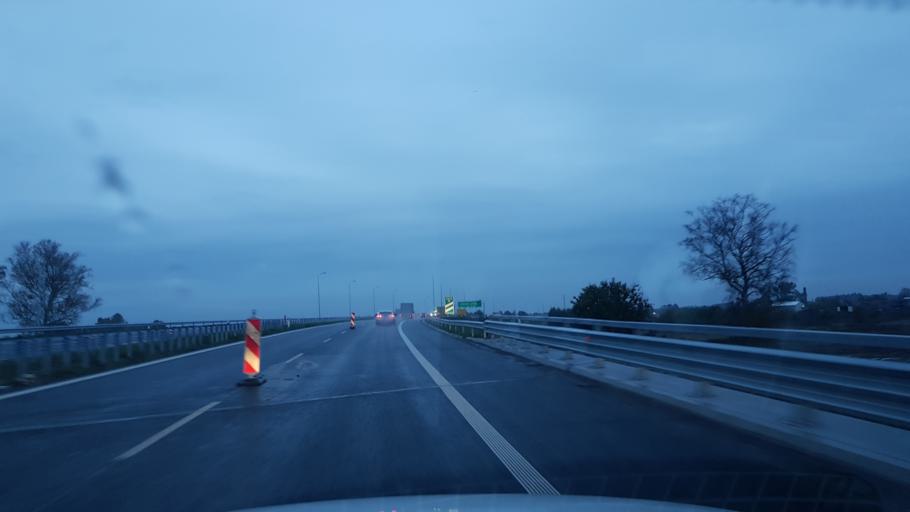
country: PL
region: West Pomeranian Voivodeship
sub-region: Powiat gryficki
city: Ploty
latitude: 53.8124
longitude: 15.2484
